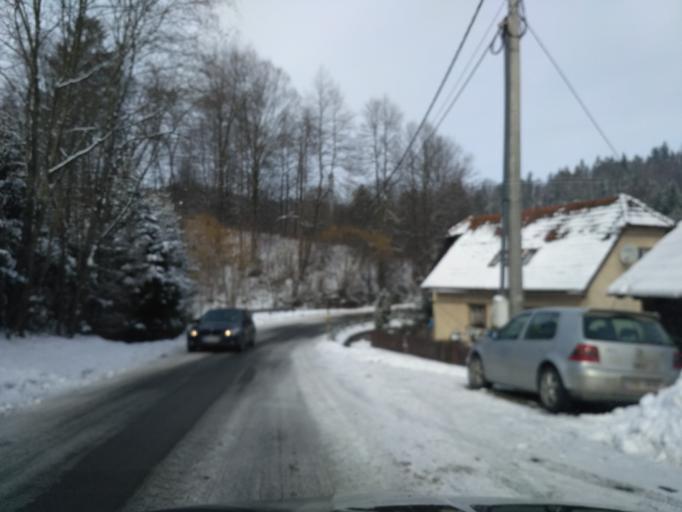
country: CZ
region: Zlin
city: Vidce
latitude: 49.4212
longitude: 18.0848
